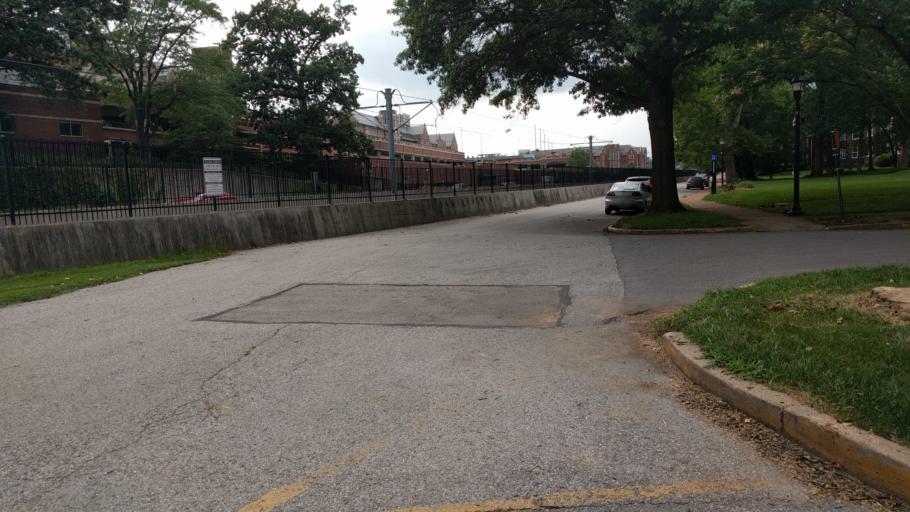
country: US
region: Missouri
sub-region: Saint Louis County
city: University City
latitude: 38.6504
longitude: -90.3074
